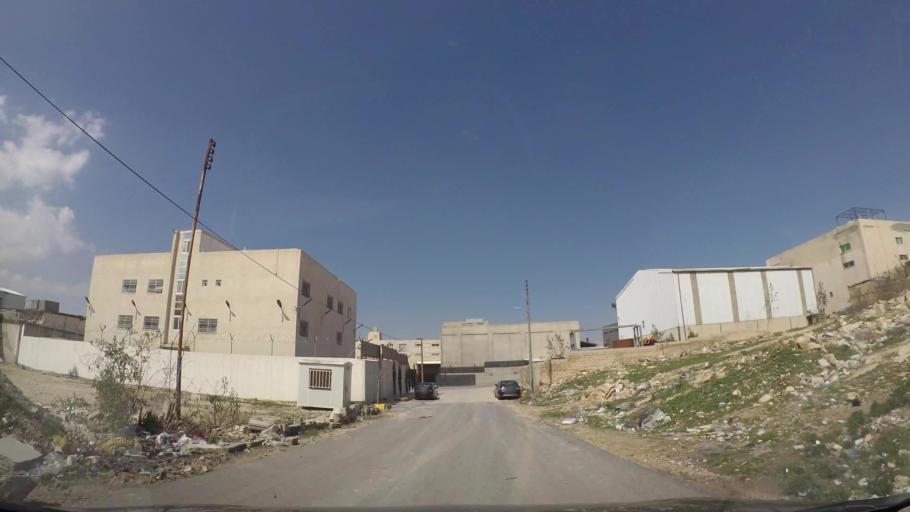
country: JO
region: Zarqa
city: Russeifa
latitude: 31.9871
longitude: 36.0133
